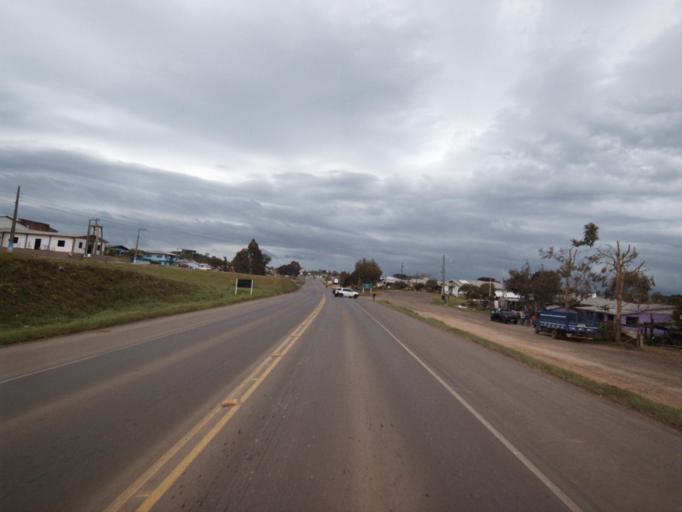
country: BR
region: Santa Catarina
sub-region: Concordia
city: Concordia
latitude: -27.0168
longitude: -51.8823
